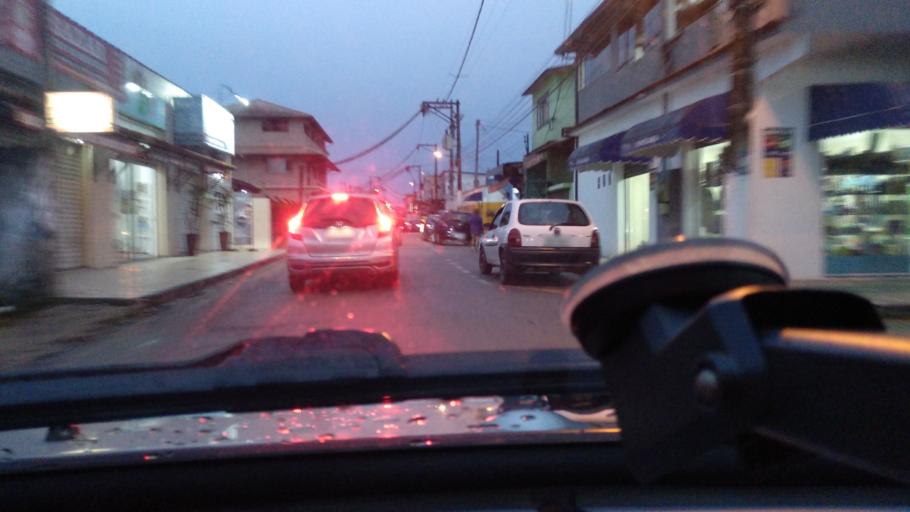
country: BR
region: Rio de Janeiro
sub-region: Angra Dos Reis
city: Angra dos Reis
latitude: -23.0141
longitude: -44.5368
